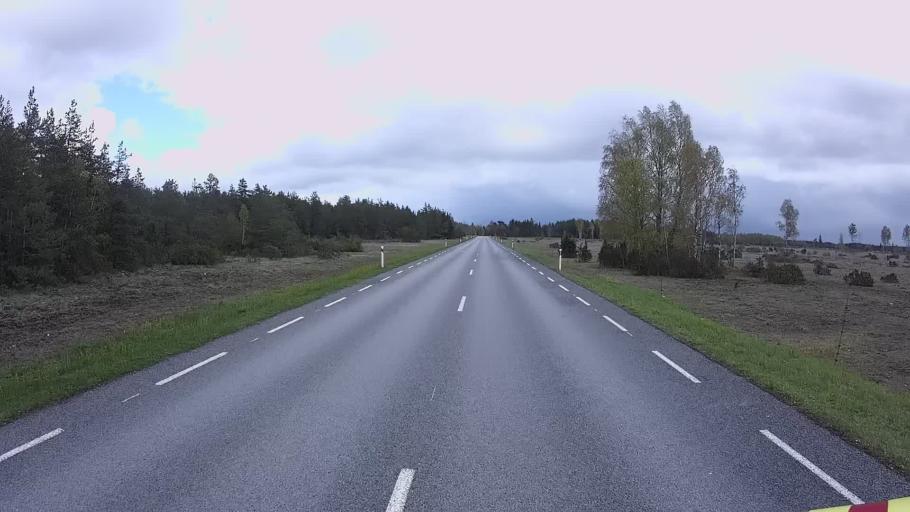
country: EE
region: Hiiumaa
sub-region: Kaerdla linn
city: Kardla
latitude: 58.8659
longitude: 22.9873
